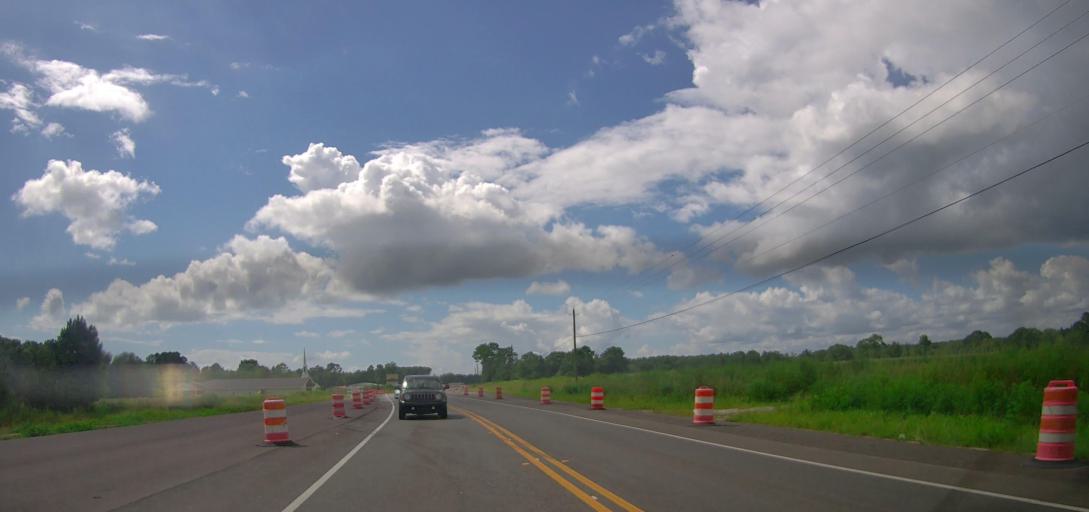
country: US
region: Georgia
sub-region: Coffee County
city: Douglas
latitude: 31.5428
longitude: -82.9296
